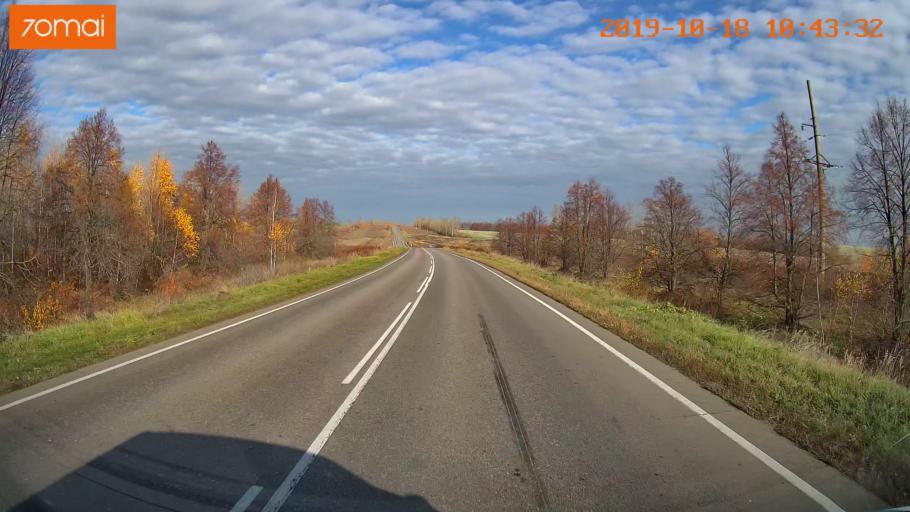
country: RU
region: Tula
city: Kurkino
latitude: 53.6408
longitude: 38.6835
